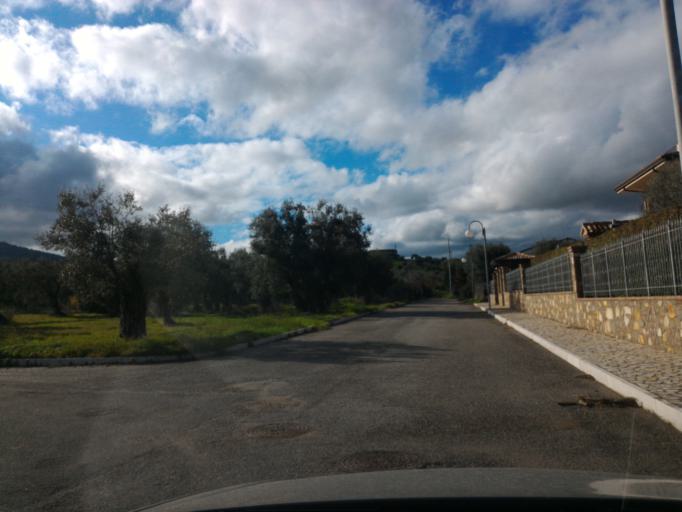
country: IT
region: Calabria
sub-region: Provincia di Crotone
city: Torretta
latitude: 39.4617
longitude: 17.0320
